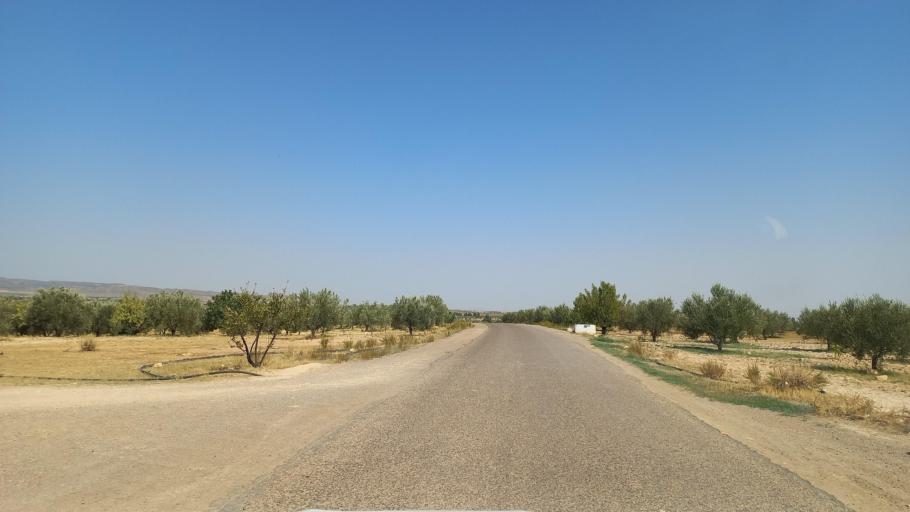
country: TN
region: Al Qasrayn
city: Kasserine
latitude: 35.2184
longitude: 9.0431
